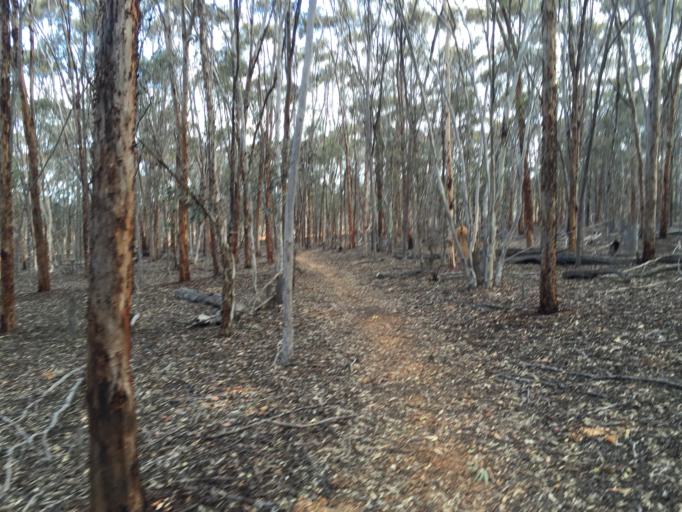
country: AU
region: Western Australia
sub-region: Narrogin
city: Narrogin
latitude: -32.7827
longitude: 116.9624
